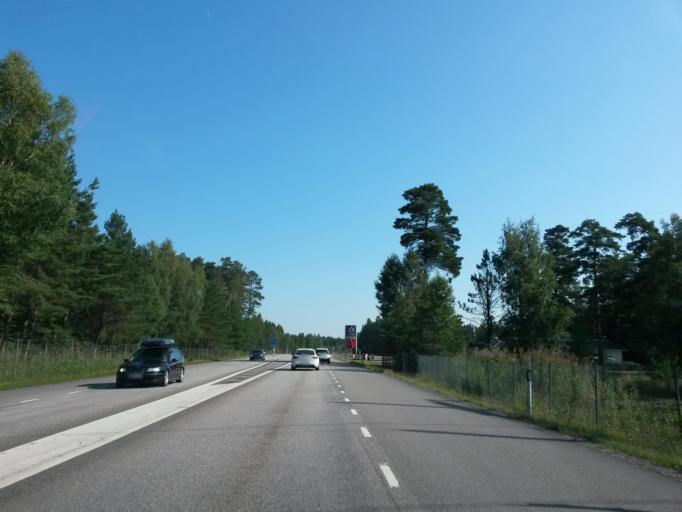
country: SE
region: Vaestra Goetaland
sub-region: Vara Kommun
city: Vara
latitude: 58.2151
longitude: 12.9117
